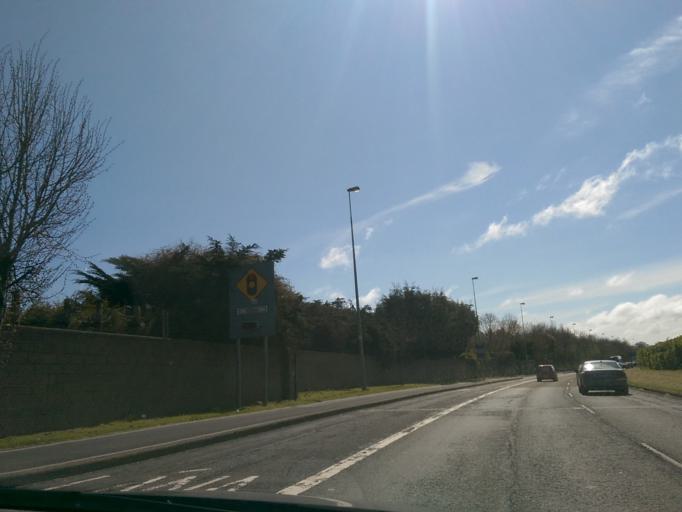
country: IE
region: Leinster
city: Cabinteely
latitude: 53.2596
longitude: -6.1466
